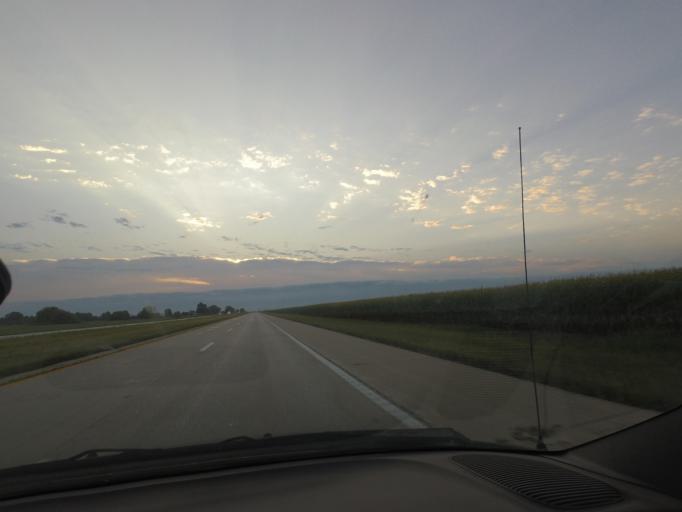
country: US
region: Missouri
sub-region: Macon County
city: Macon
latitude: 39.7501
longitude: -92.3430
